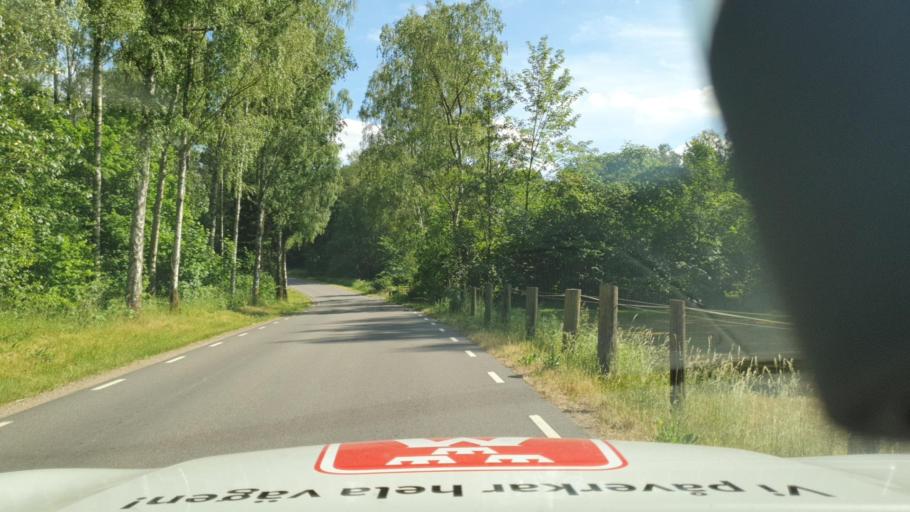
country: SE
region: Skane
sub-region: Sjobo Kommun
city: Blentarp
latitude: 55.5693
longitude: 13.5708
